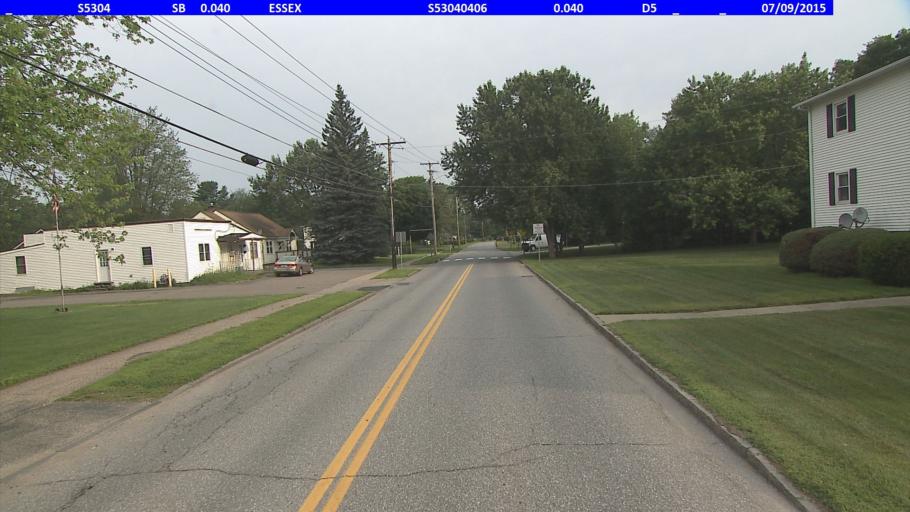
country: US
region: Vermont
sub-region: Chittenden County
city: Essex Junction
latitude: 44.4983
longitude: -73.1318
